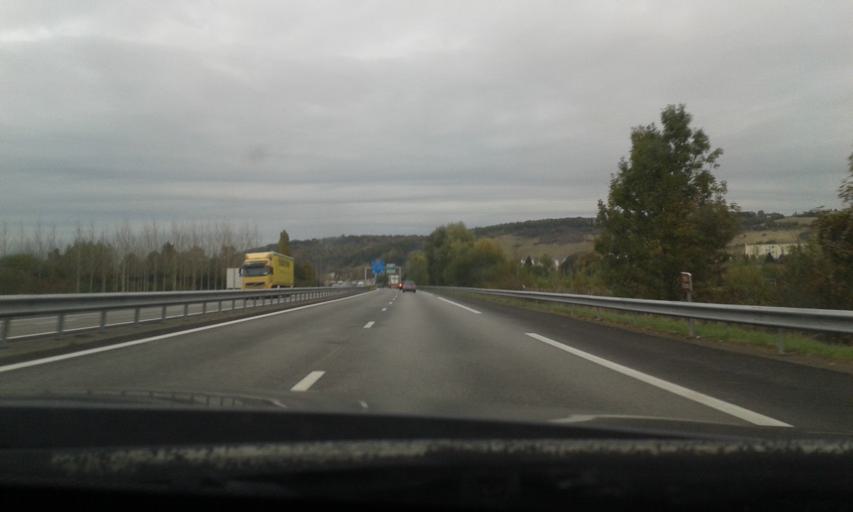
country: FR
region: Haute-Normandie
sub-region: Departement de l'Eure
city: Louviers
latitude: 49.2021
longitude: 1.1778
